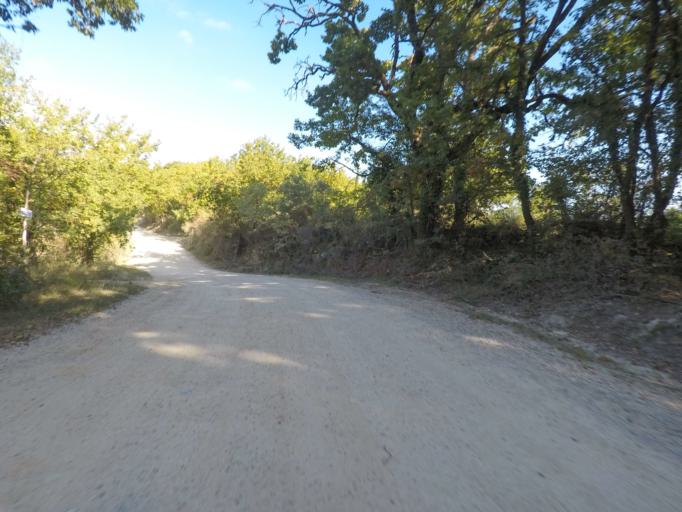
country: IT
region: Tuscany
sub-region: Provincia di Siena
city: Castellina in Chianti
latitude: 43.4377
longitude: 11.3115
